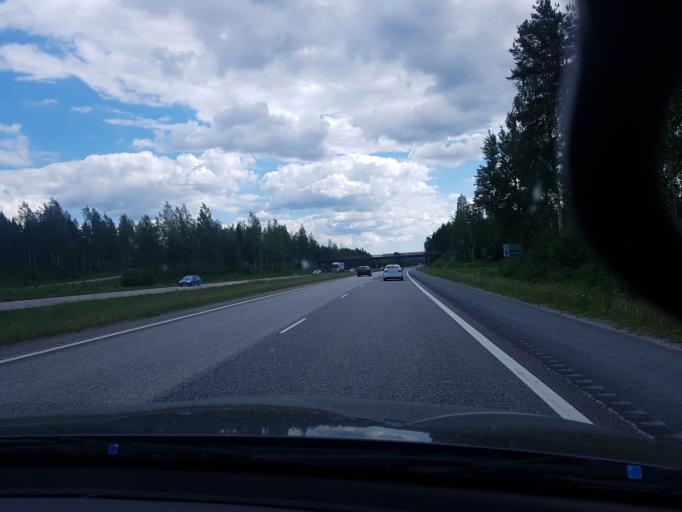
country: FI
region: Haeme
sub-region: Riihimaeki
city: Riihimaeki
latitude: 60.6627
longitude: 24.7915
